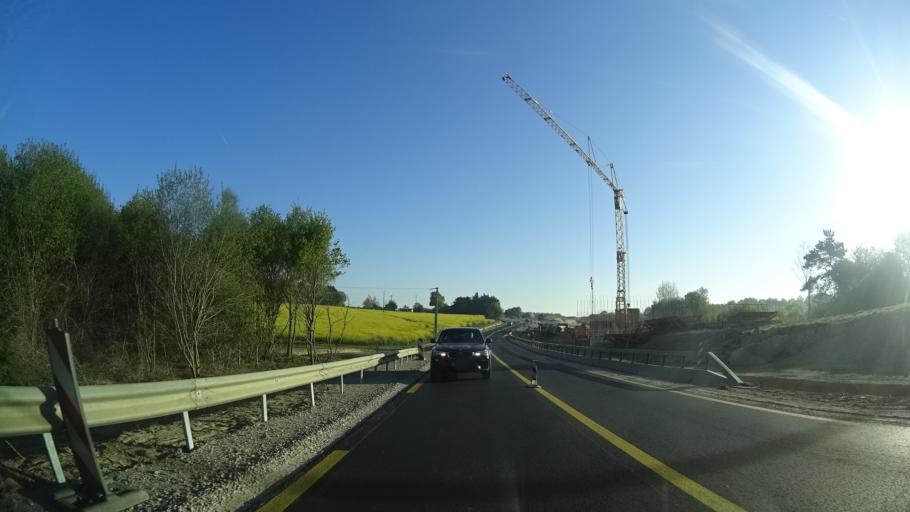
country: FR
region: Brittany
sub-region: Departement d'Ille-et-Vilaine
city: Saint-Just
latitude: 47.7736
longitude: -1.9332
